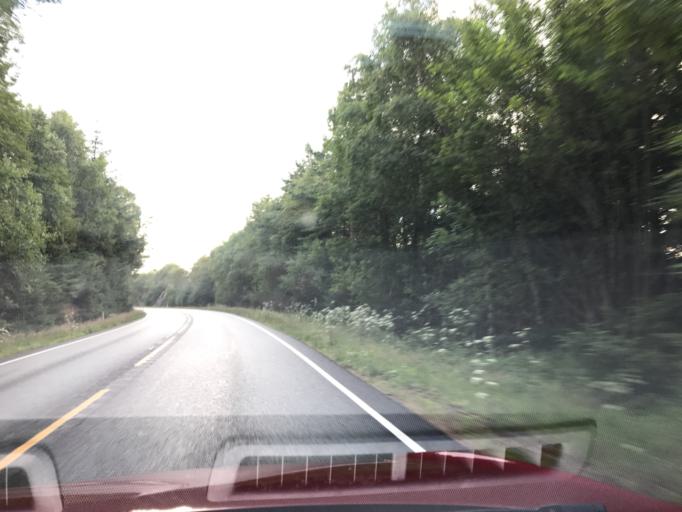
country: NO
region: Hordaland
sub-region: Sveio
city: Sveio
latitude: 59.5418
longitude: 5.3619
